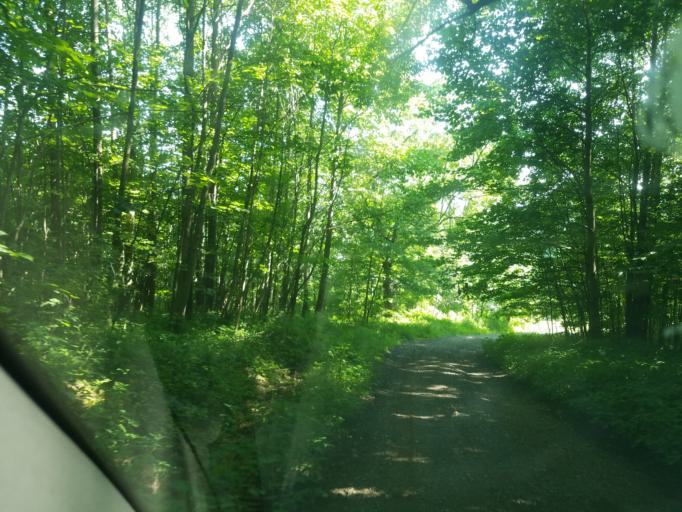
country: US
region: Ohio
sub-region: Sandusky County
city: Bellville
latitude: 40.5972
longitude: -82.5704
